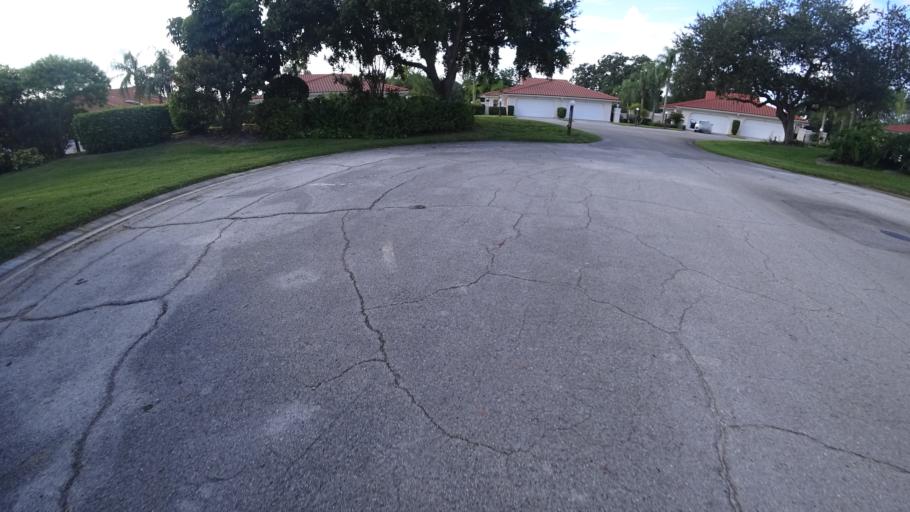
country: US
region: Florida
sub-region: Sarasota County
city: Desoto Lakes
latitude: 27.4095
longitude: -82.4923
